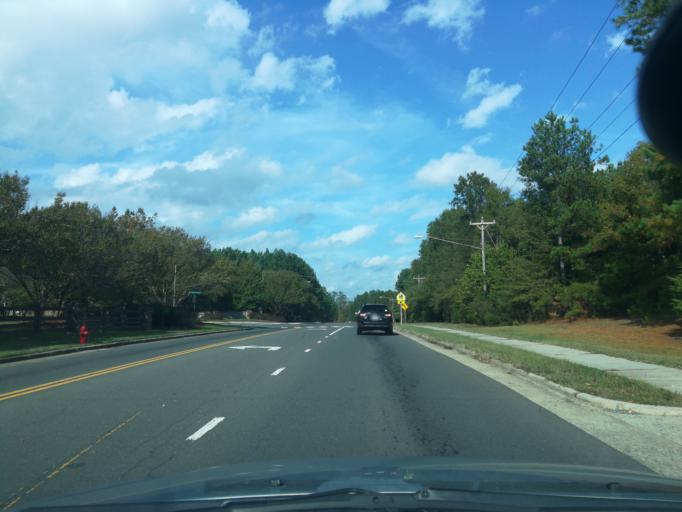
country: US
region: North Carolina
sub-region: Durham County
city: Durham
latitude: 36.0509
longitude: -78.9355
